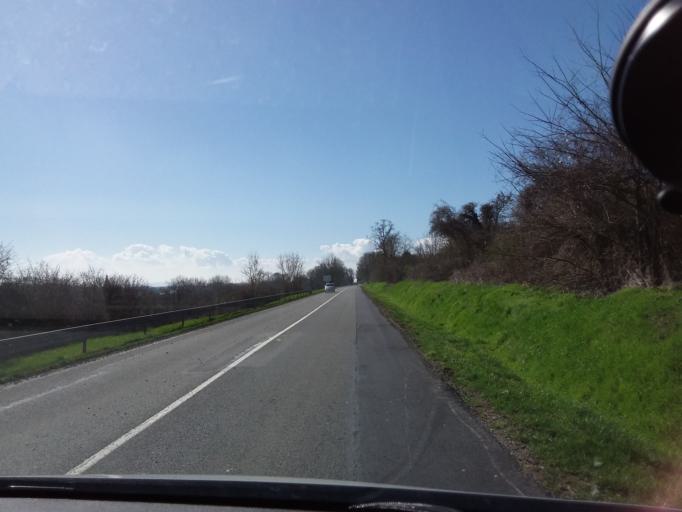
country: FR
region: Picardie
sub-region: Departement de l'Aisne
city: Guignicourt
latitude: 49.4388
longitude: 4.0350
